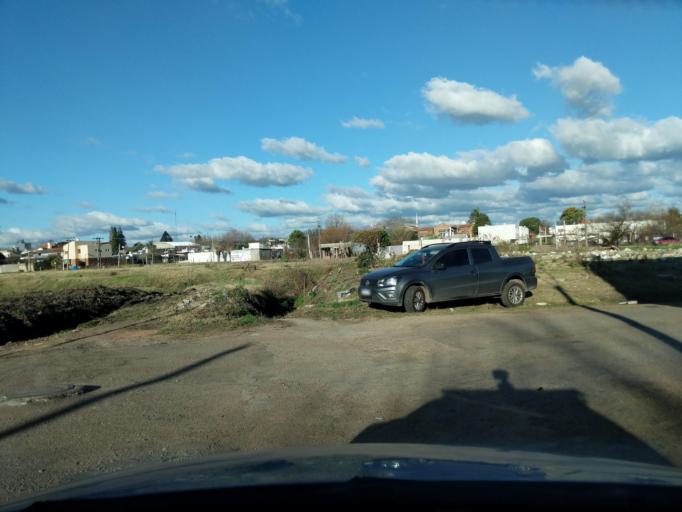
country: UY
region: Florida
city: Florida
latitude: -34.1005
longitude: -56.2241
